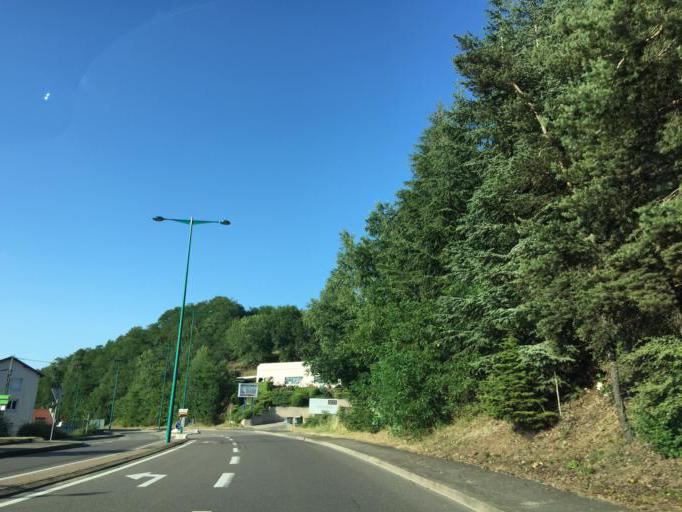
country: FR
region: Rhone-Alpes
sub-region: Departement de la Loire
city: La Talaudiere
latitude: 45.4606
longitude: 4.4268
